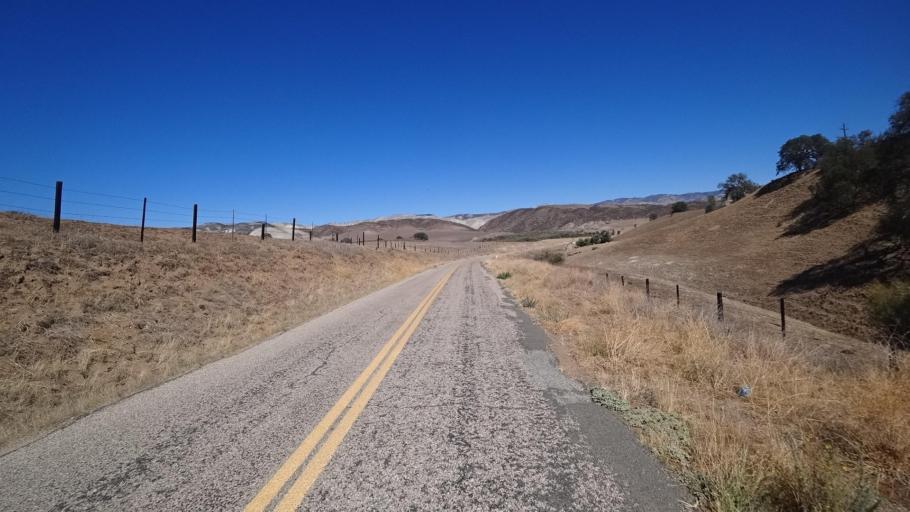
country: US
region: California
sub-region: Monterey County
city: King City
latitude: 36.2638
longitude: -120.9961
